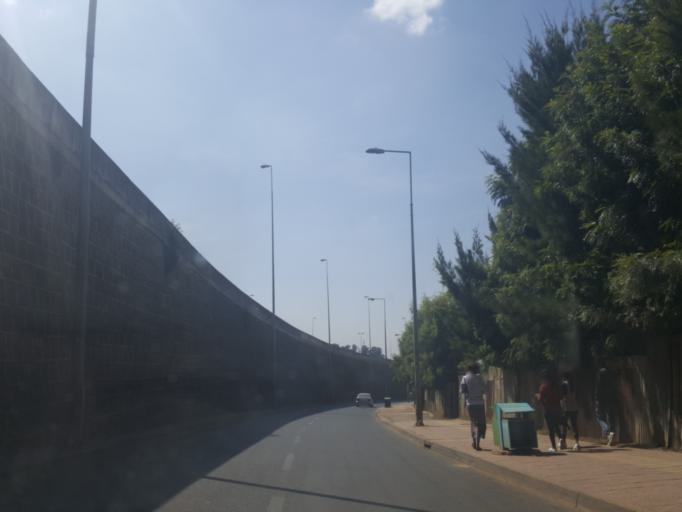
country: ET
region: Adis Abeba
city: Addis Ababa
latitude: 9.0590
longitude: 38.7142
